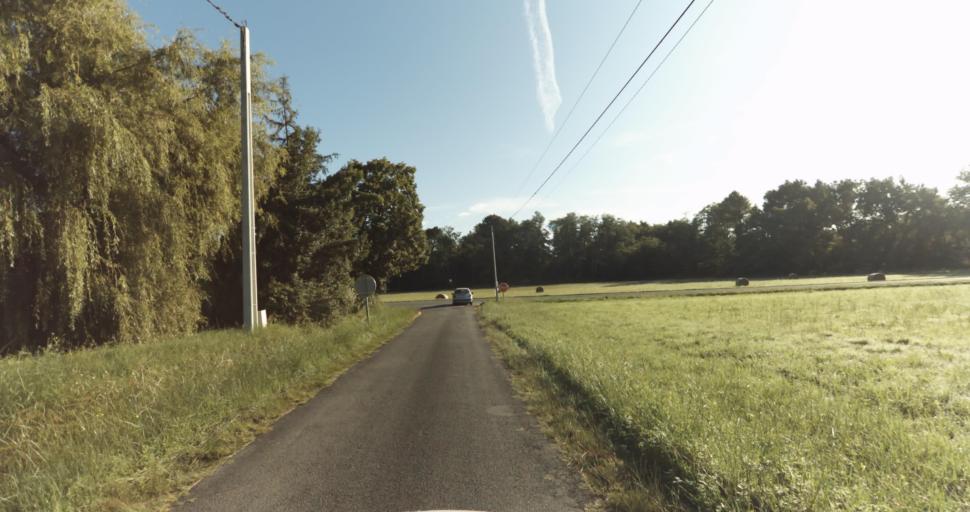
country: FR
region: Aquitaine
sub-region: Departement de la Gironde
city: Bazas
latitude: 44.4113
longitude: -0.2129
